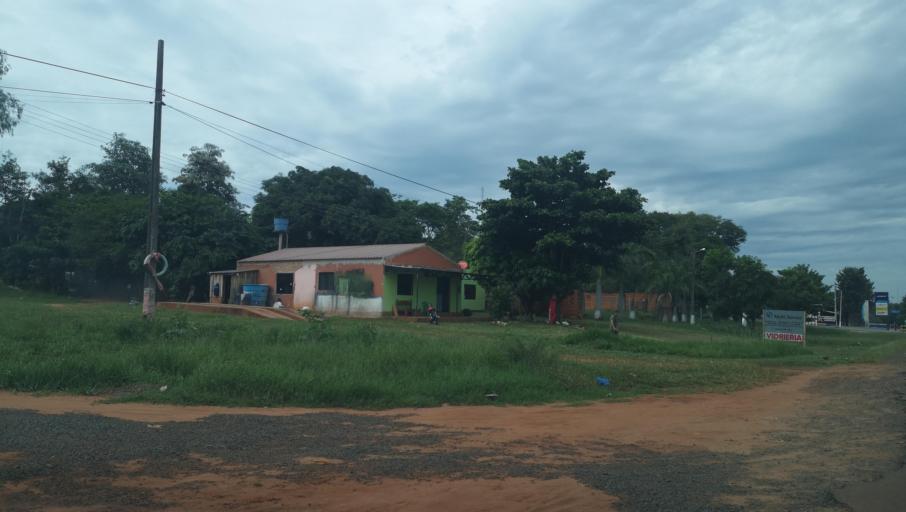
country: PY
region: San Pedro
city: Capiibary
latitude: -24.7157
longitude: -56.0119
